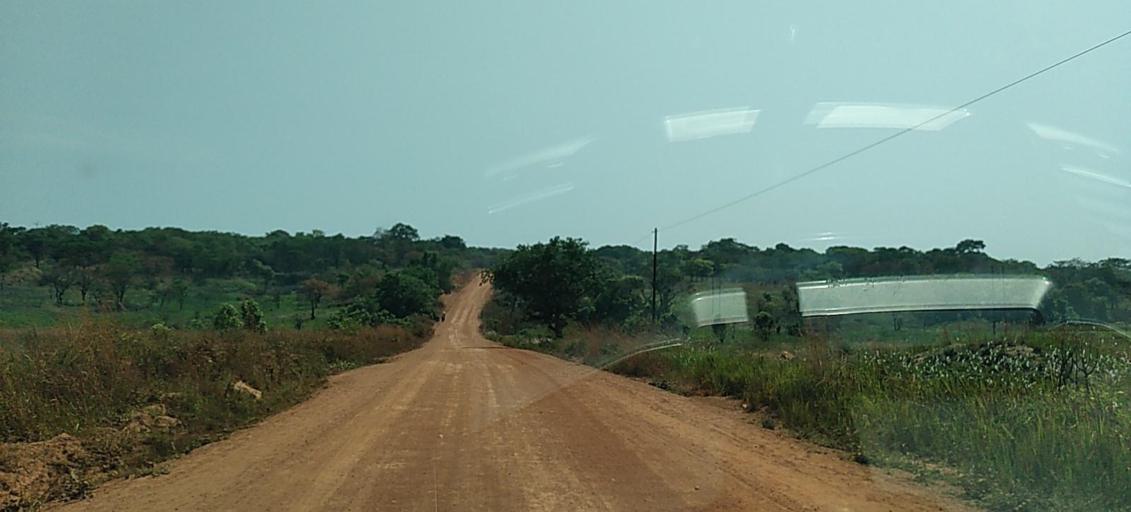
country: ZM
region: North-Western
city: Kansanshi
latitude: -11.9966
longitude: 26.6147
